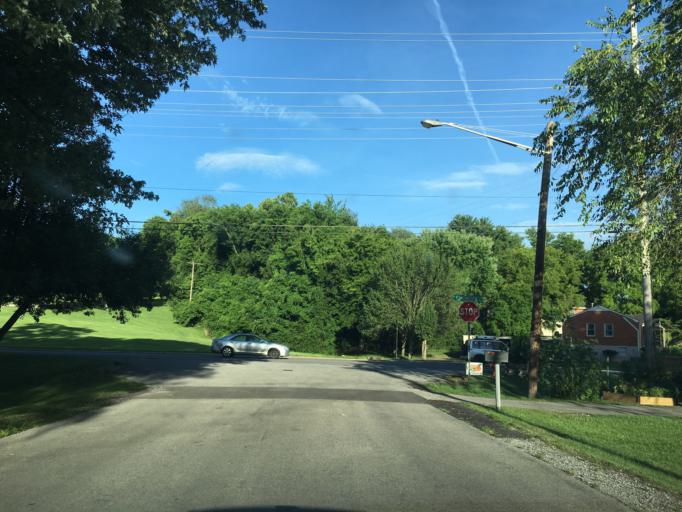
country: US
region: Tennessee
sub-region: Davidson County
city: Oak Hill
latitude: 36.0678
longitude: -86.7377
